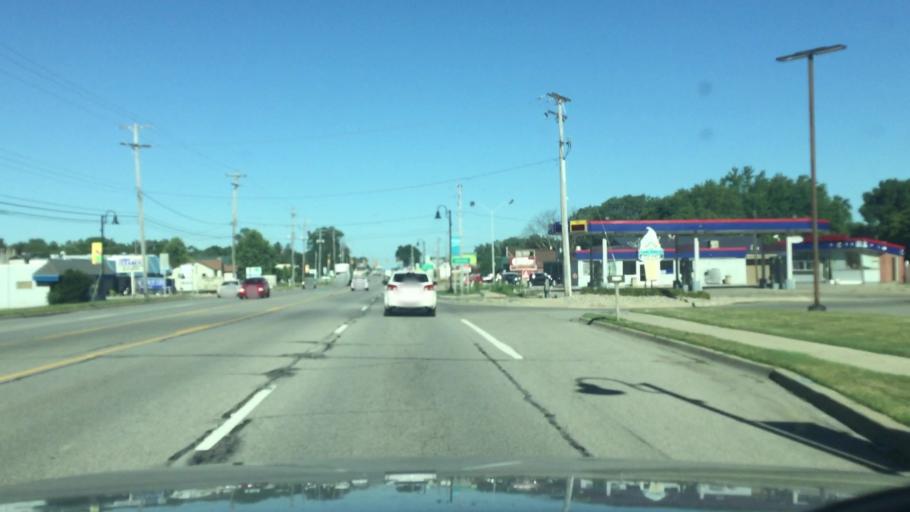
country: US
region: Michigan
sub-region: Saginaw County
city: Shields
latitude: 43.4158
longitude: -84.0483
